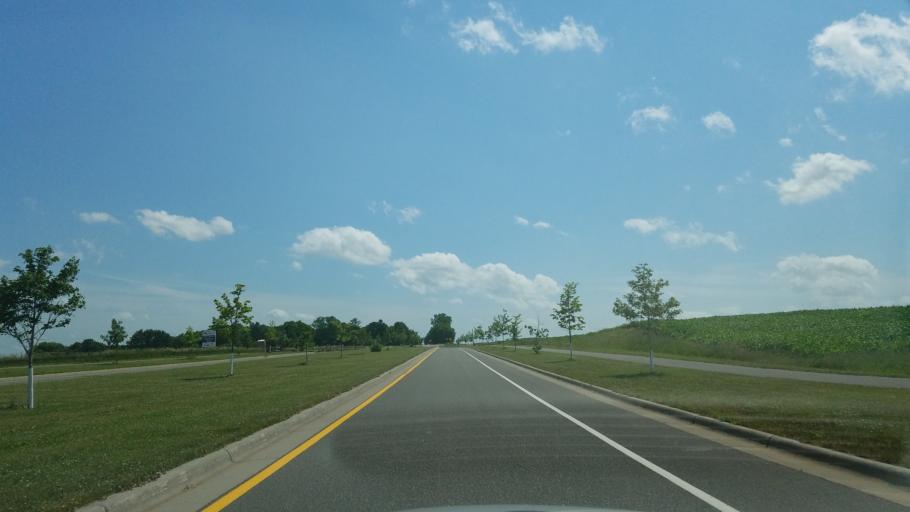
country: US
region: Minnesota
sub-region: Washington County
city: Cottage Grove
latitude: 44.8795
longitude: -92.9238
